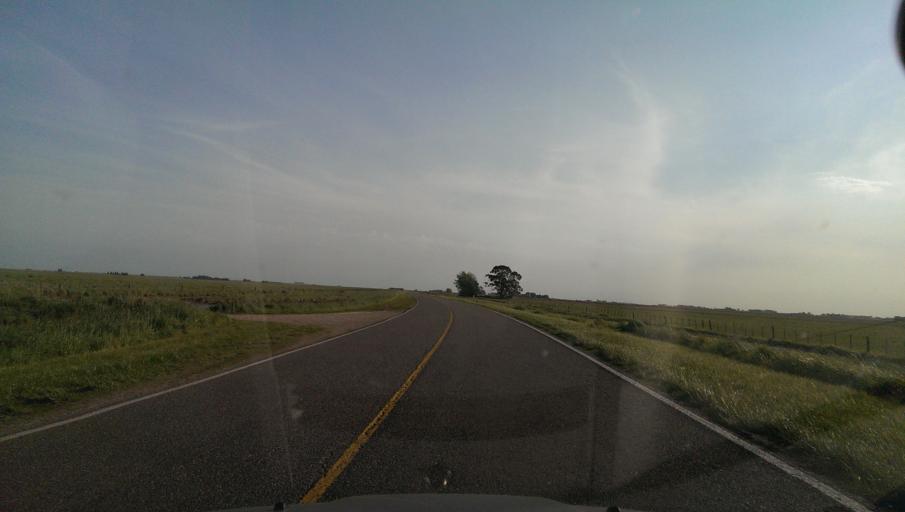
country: AR
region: Buenos Aires
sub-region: Partido de General La Madrid
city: General La Madrid
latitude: -37.5248
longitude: -61.2425
